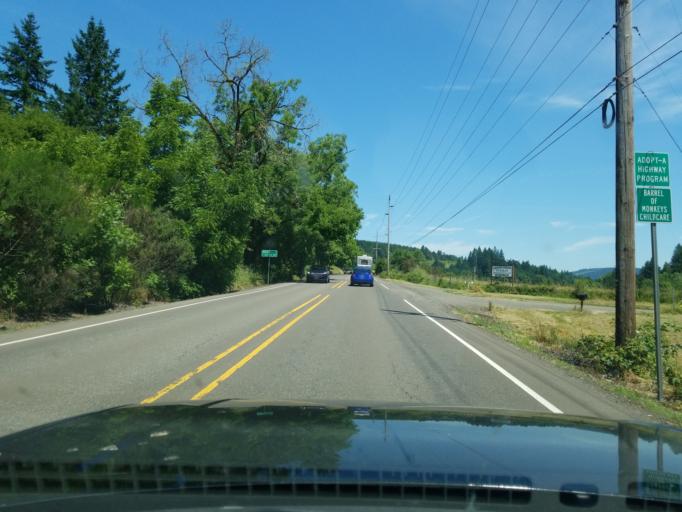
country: US
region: Oregon
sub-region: Yamhill County
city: Yamhill
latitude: 45.3895
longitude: -123.1373
